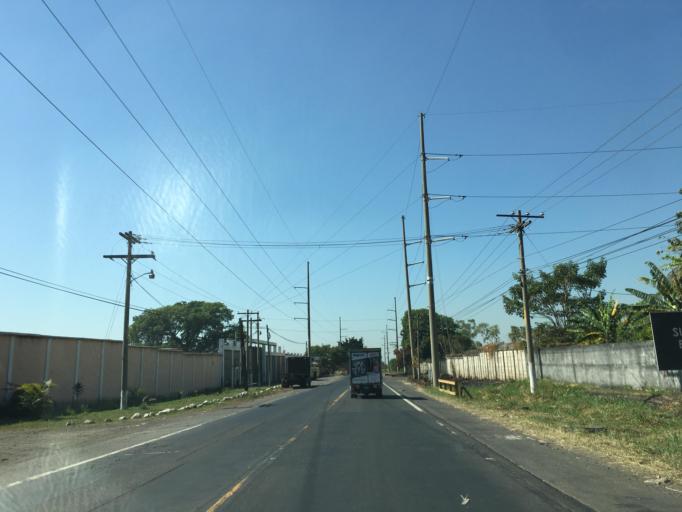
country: GT
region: Escuintla
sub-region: Municipio de Escuintla
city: Escuintla
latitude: 14.2614
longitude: -90.7972
